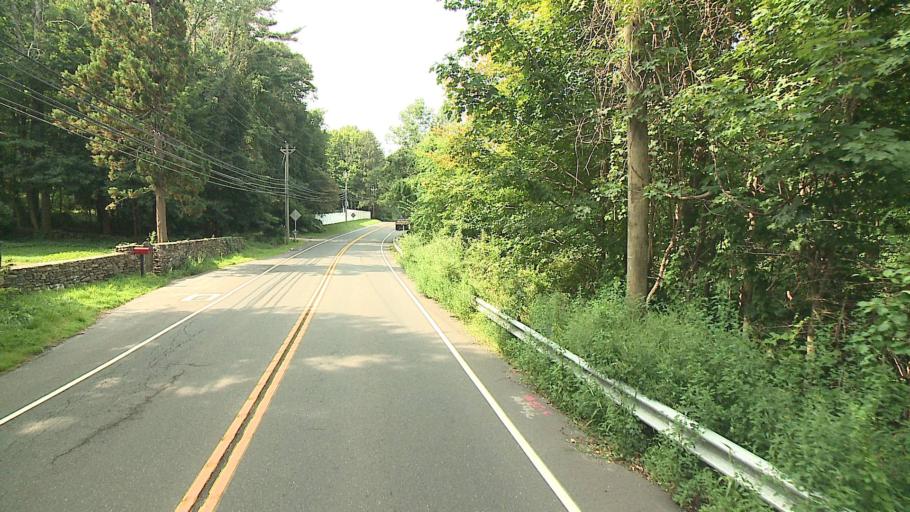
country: US
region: Connecticut
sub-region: Fairfield County
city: Georgetown
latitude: 41.2760
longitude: -73.4173
